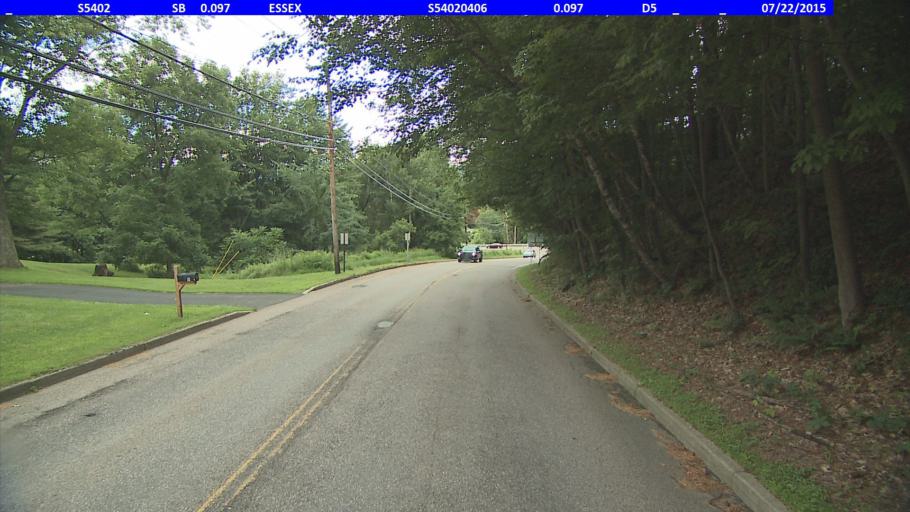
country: US
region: Vermont
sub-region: Chittenden County
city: Williston
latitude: 44.4804
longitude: -73.0495
